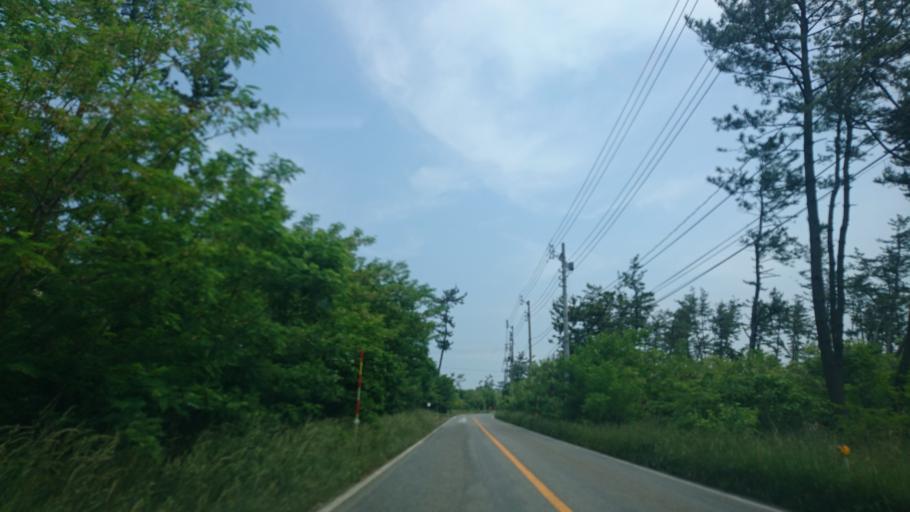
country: JP
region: Niigata
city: Shibata
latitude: 38.0501
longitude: 139.3180
